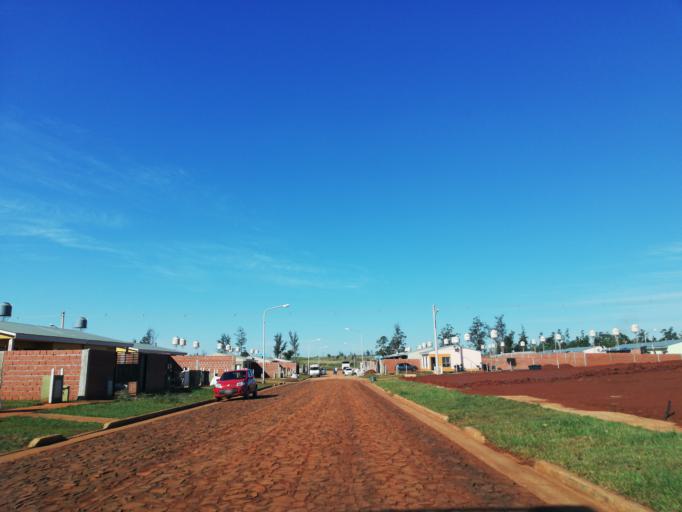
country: AR
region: Misiones
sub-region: Departamento de Capital
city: Posadas
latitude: -27.4161
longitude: -55.9904
